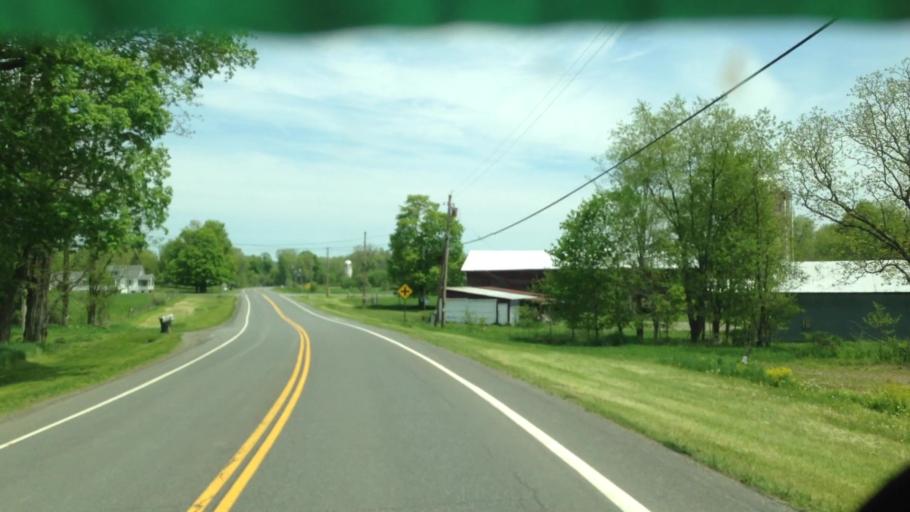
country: US
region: New York
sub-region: Dutchess County
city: Pine Plains
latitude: 42.0678
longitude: -73.6192
